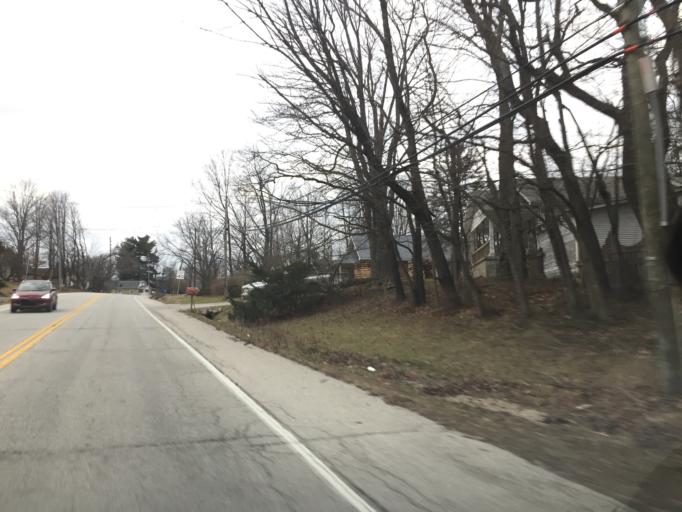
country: US
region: Indiana
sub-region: Monroe County
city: Bloomington
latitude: 39.1810
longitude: -86.5492
